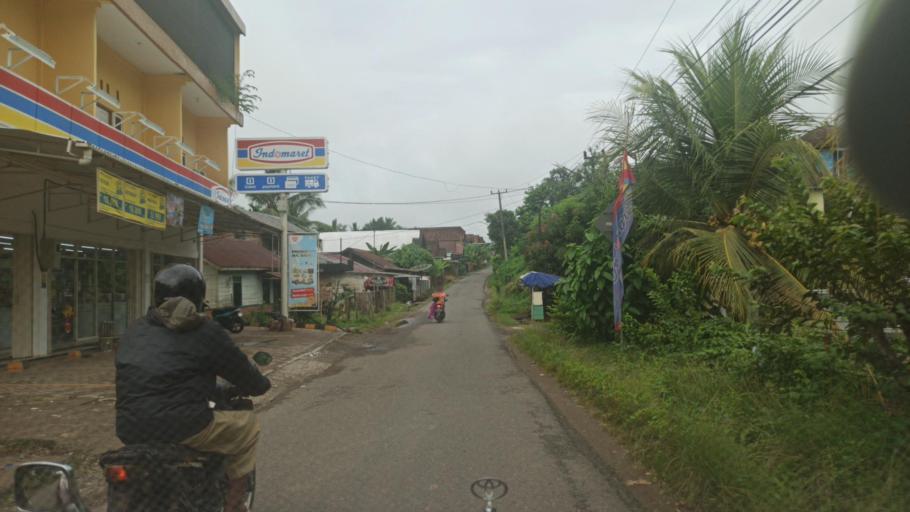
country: ID
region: South Sumatra
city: Gunungmegang Dalam
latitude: -3.2661
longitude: 103.8158
